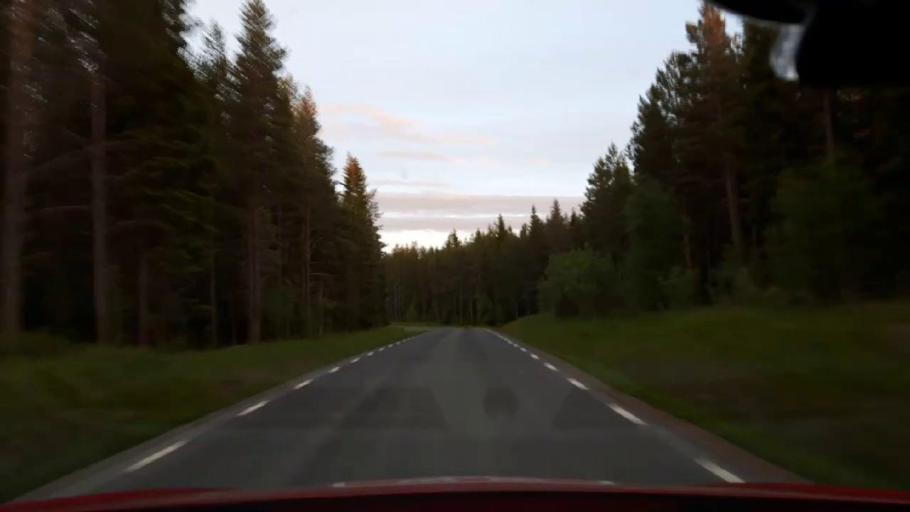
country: SE
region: Jaemtland
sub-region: OEstersunds Kommun
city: Brunflo
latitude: 63.0635
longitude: 14.8035
